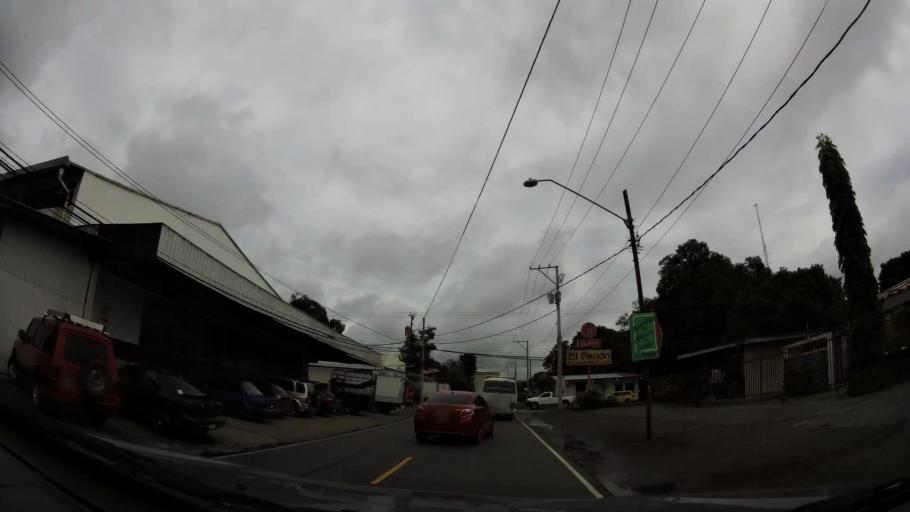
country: PA
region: Chiriqui
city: David
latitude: 8.4332
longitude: -82.4286
